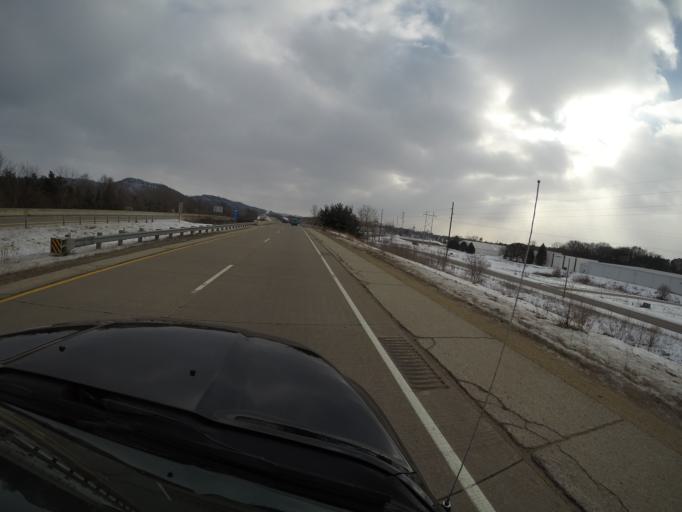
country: US
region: Wisconsin
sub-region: La Crosse County
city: Onalaska
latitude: 43.9134
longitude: -91.2360
